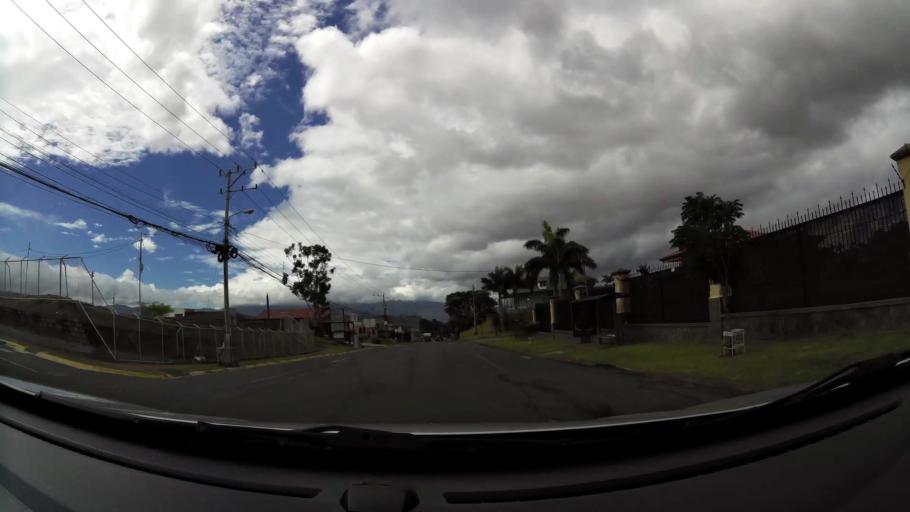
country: CR
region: Cartago
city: San Diego
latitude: 9.9093
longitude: -84.0038
